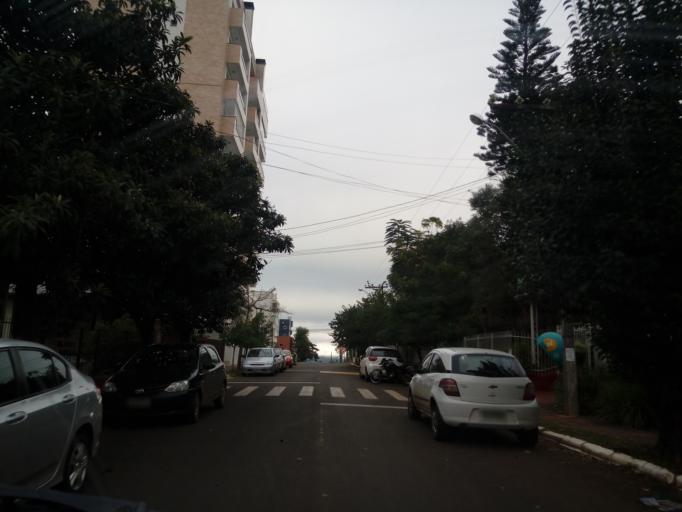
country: BR
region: Santa Catarina
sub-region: Chapeco
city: Chapeco
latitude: -27.0938
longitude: -52.6302
